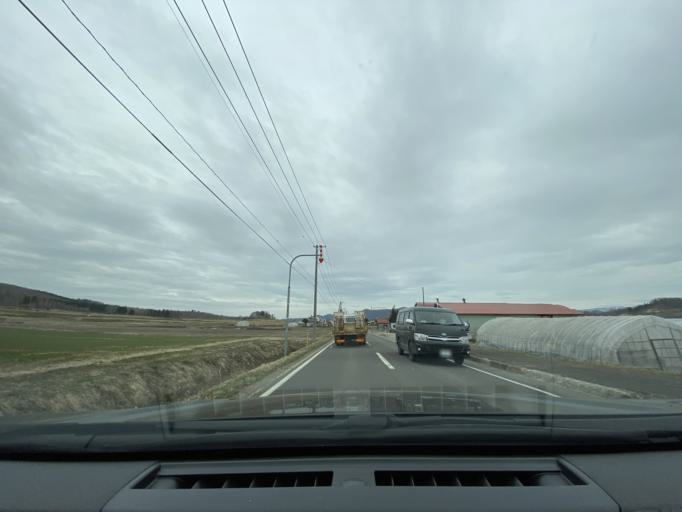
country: JP
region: Hokkaido
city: Nayoro
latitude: 44.0973
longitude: 142.4746
